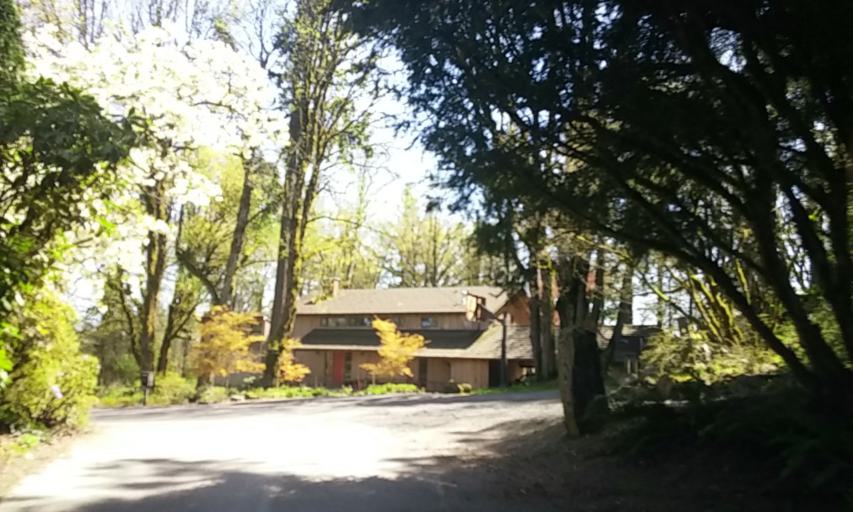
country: US
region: Oregon
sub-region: Washington County
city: West Haven-Sylvan
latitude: 45.5267
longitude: -122.7524
